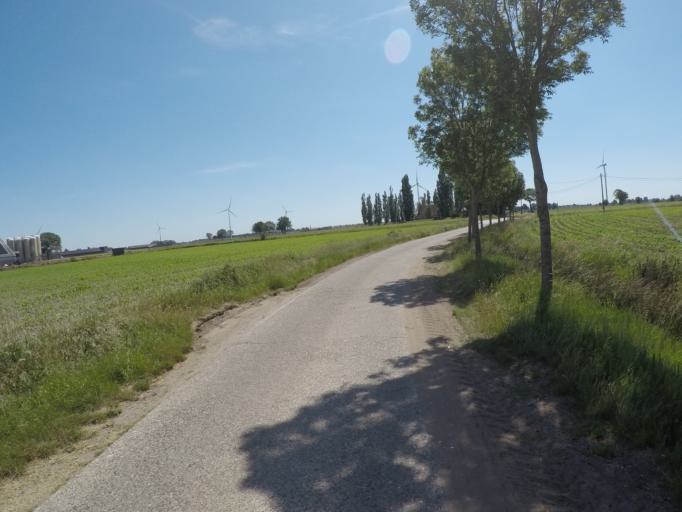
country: NL
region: North Brabant
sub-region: Gemeente Zundert
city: Zundert
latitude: 51.4091
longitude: 4.6745
